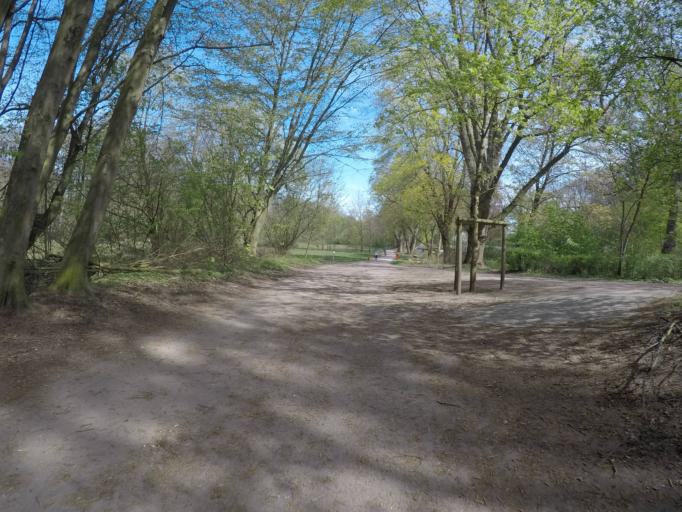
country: DE
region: Hamburg
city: Ohlsdorf
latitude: 53.6332
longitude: 10.0437
